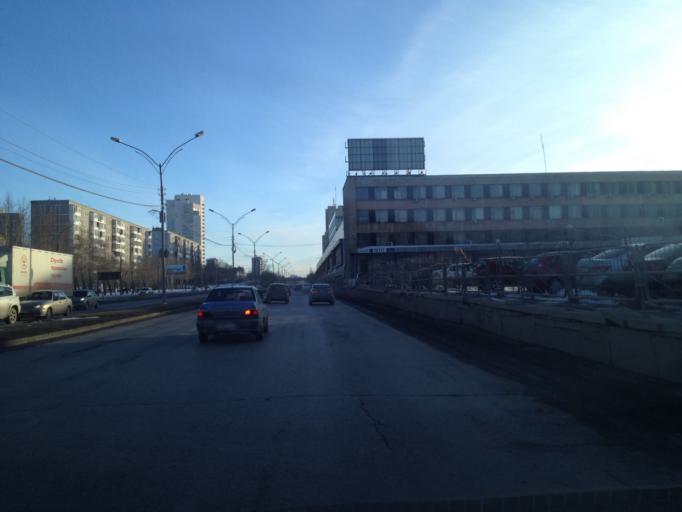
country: RU
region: Sverdlovsk
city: Sovkhoznyy
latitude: 56.8188
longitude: 60.5568
